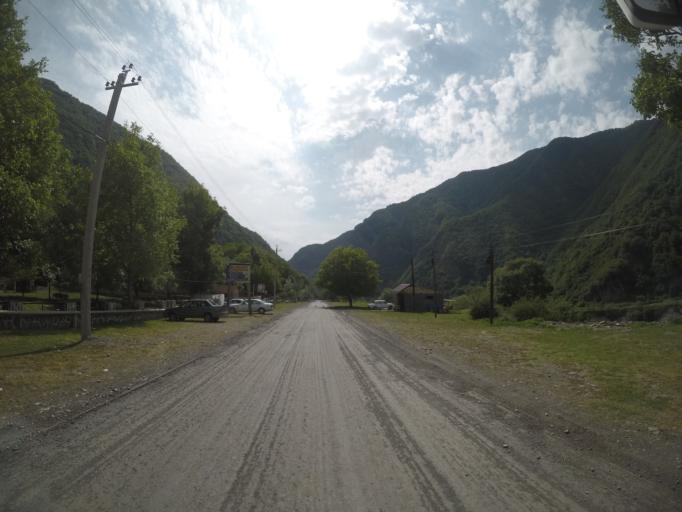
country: AZ
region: Qakh Rayon
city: Qaxbas
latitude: 41.4655
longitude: 47.0446
